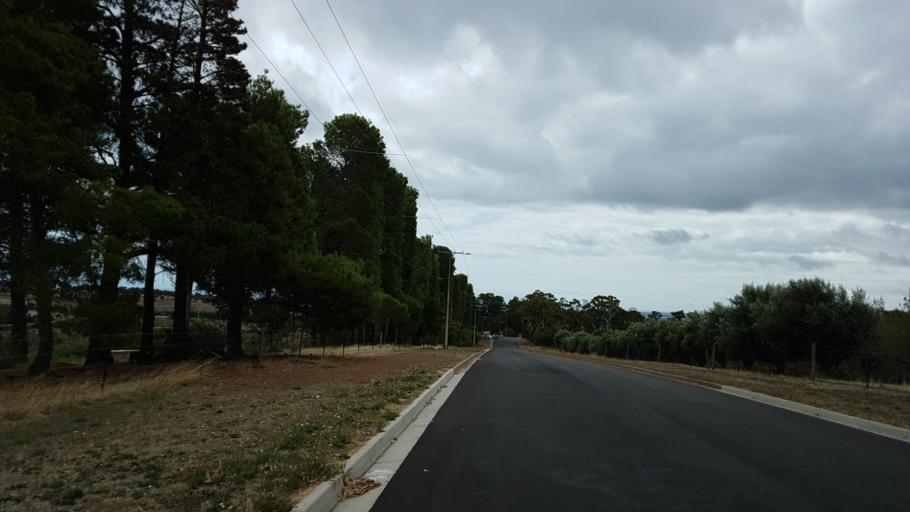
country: AU
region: South Australia
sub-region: Onkaparinga
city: Bedford Park
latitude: -35.0432
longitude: 138.5660
